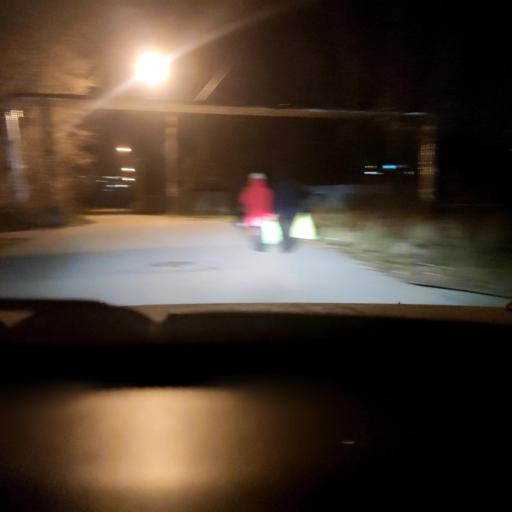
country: RU
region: Perm
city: Polazna
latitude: 58.1485
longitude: 56.4362
